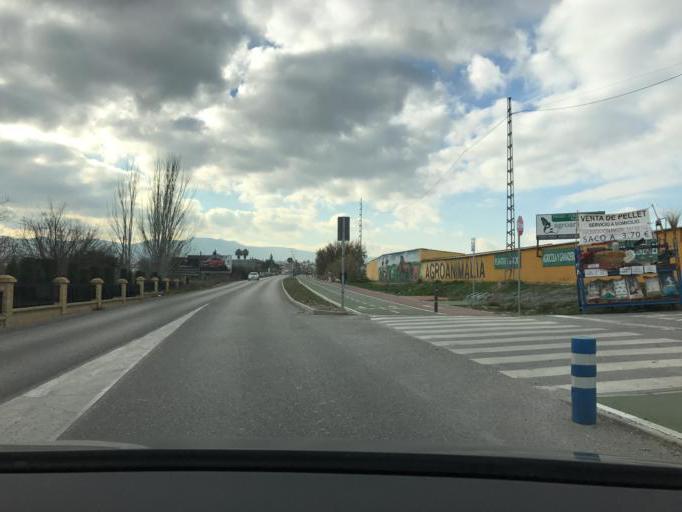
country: ES
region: Andalusia
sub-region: Provincia de Granada
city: Ogijares
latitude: 37.1328
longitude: -3.6032
